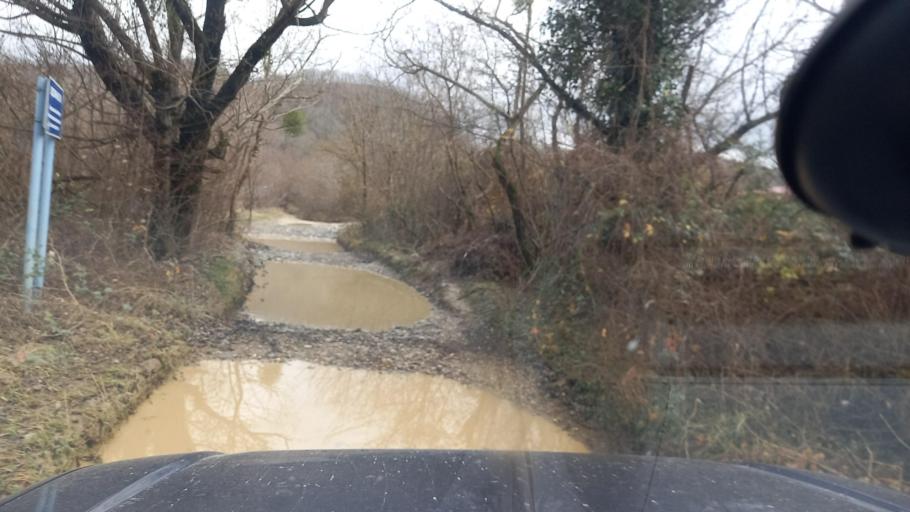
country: RU
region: Krasnodarskiy
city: Pshada
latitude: 44.4818
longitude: 38.4049
